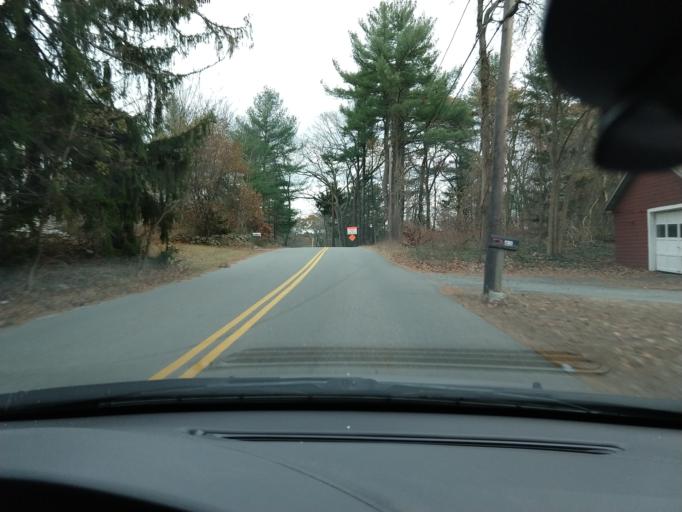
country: US
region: Massachusetts
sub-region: Middlesex County
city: Westford
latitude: 42.5878
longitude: -71.4265
